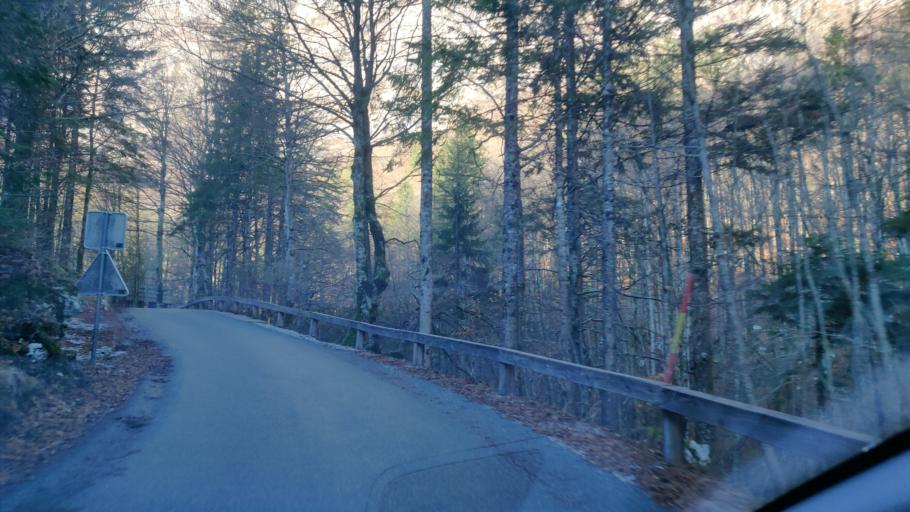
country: SI
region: Tolmin
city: Tolmin
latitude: 46.2900
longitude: 13.8040
